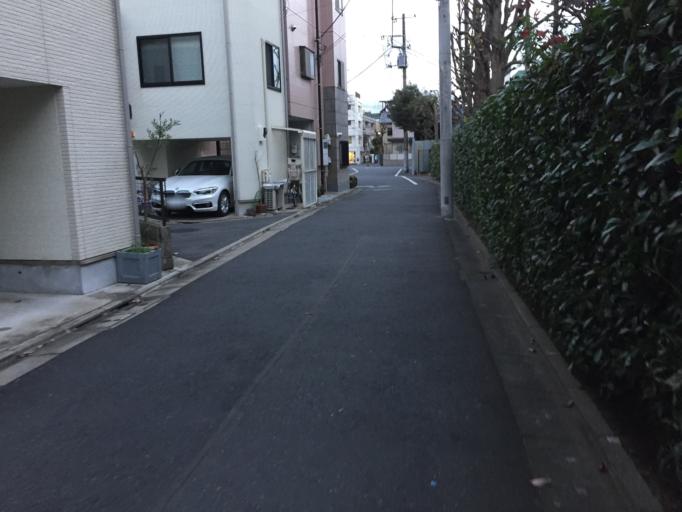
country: JP
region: Tokyo
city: Tokyo
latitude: 35.6416
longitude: 139.6741
